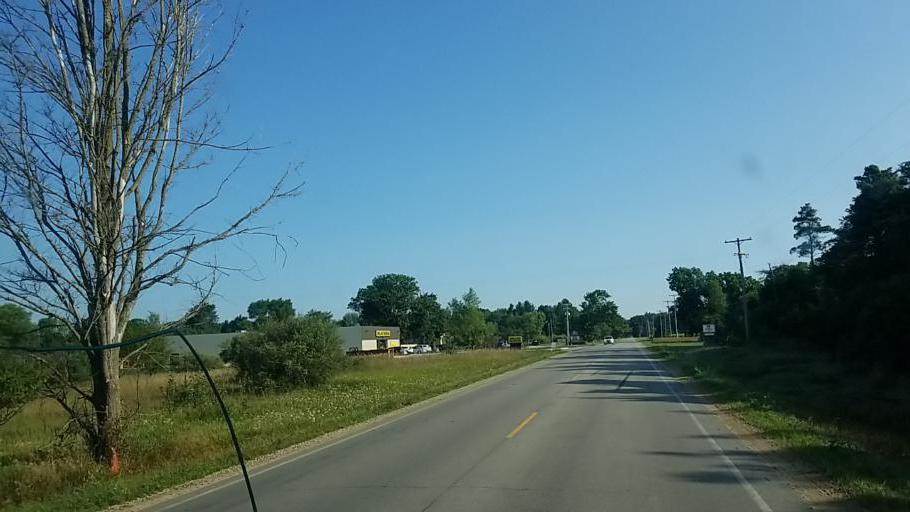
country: US
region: Michigan
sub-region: Newaygo County
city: Fremont
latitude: 43.3629
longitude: -85.9395
